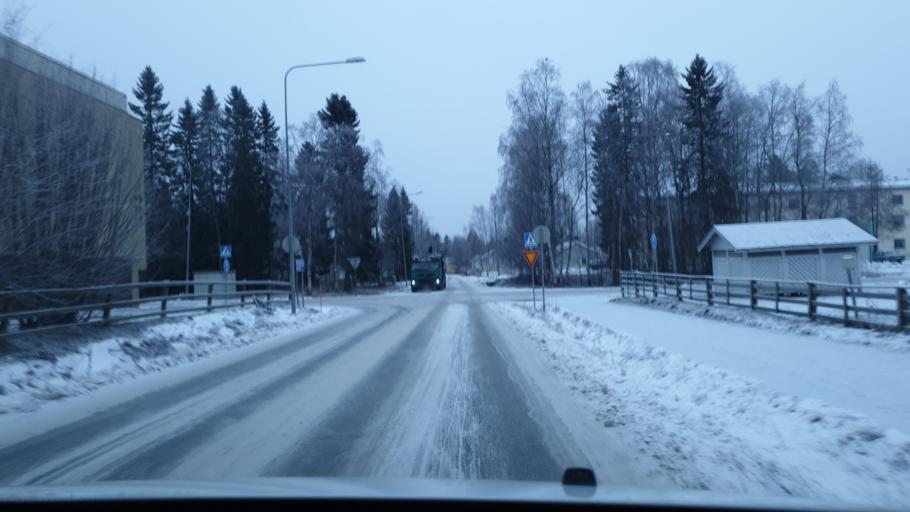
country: FI
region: Lapland
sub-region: Kemi-Tornio
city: Kemi
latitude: 65.7344
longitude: 24.6097
